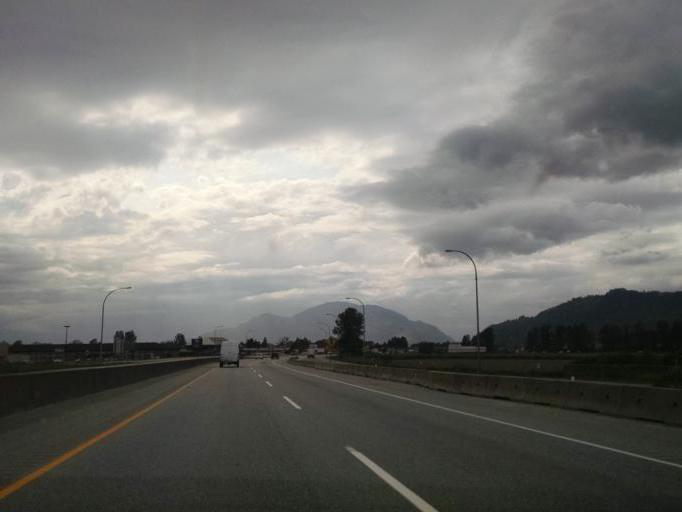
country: CA
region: British Columbia
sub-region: Fraser Valley Regional District
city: Chilliwack
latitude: 49.1446
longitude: -121.9632
